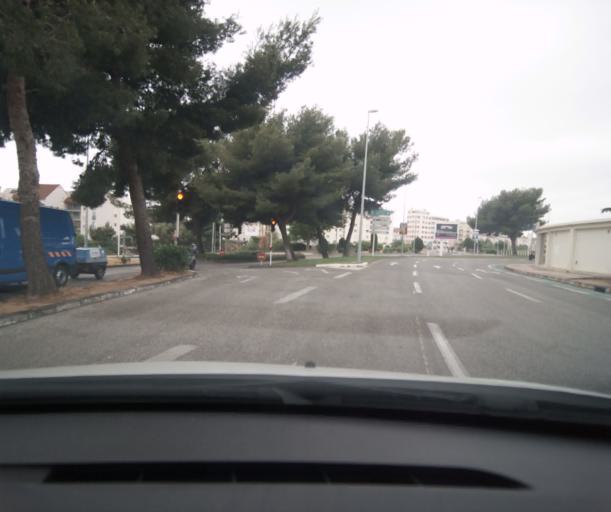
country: FR
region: Provence-Alpes-Cote d'Azur
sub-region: Departement du Var
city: Toulon
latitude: 43.1258
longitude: 5.9384
